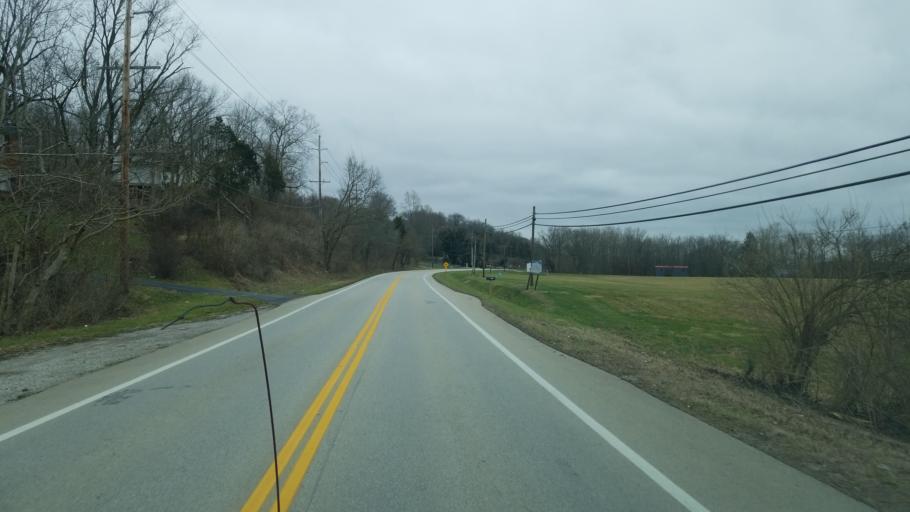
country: US
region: Ohio
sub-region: Clermont County
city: New Richmond
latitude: 38.9252
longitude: -84.2558
